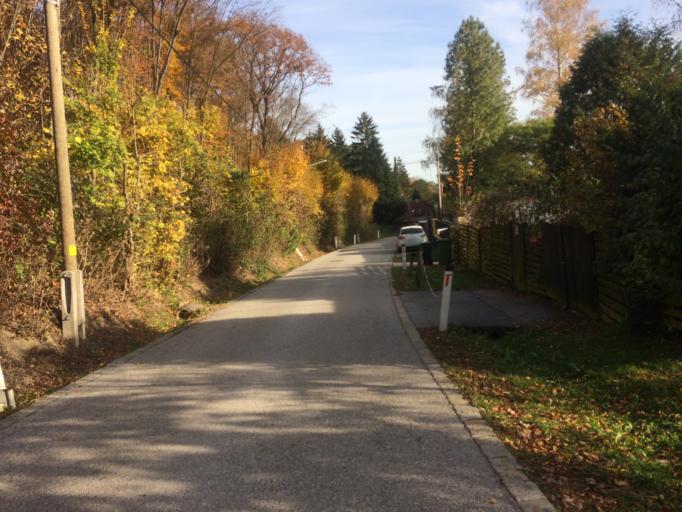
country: AT
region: Lower Austria
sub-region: Politischer Bezirk Wien-Umgebung
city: Purkersdorf
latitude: 48.2130
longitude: 16.2033
